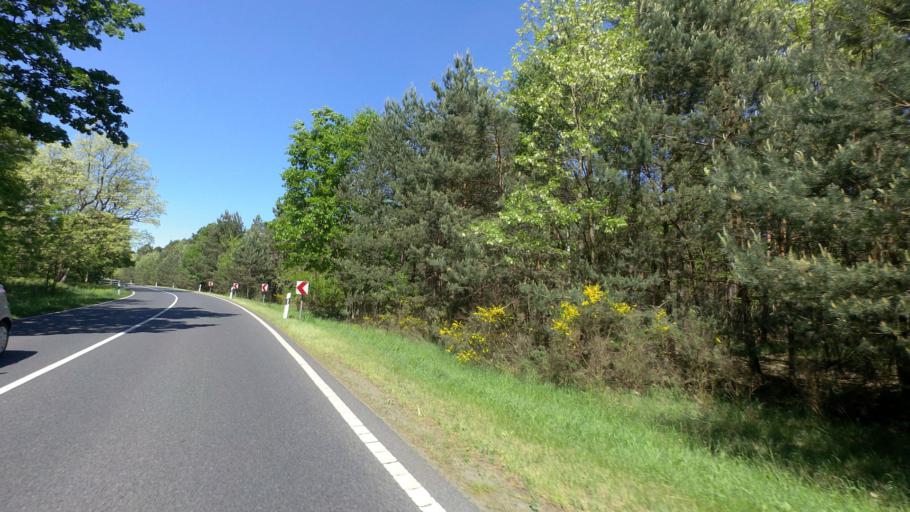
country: DE
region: Brandenburg
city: Lieberose
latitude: 51.9550
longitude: 14.3303
